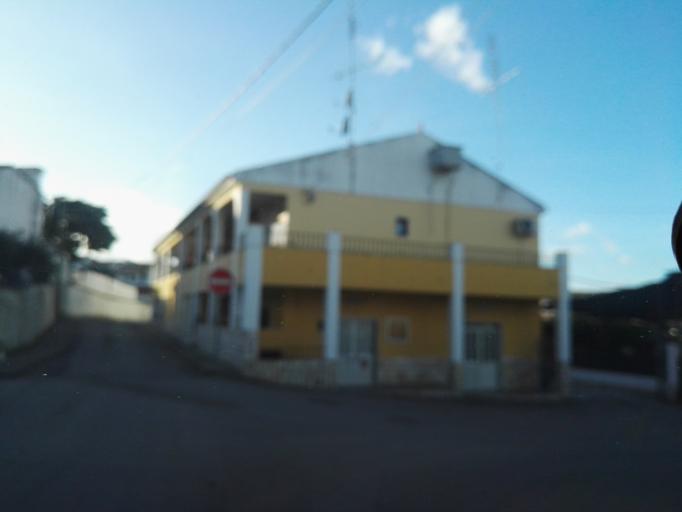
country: PT
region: Portalegre
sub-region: Elvas
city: Elvas
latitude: 38.8832
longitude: -7.1712
